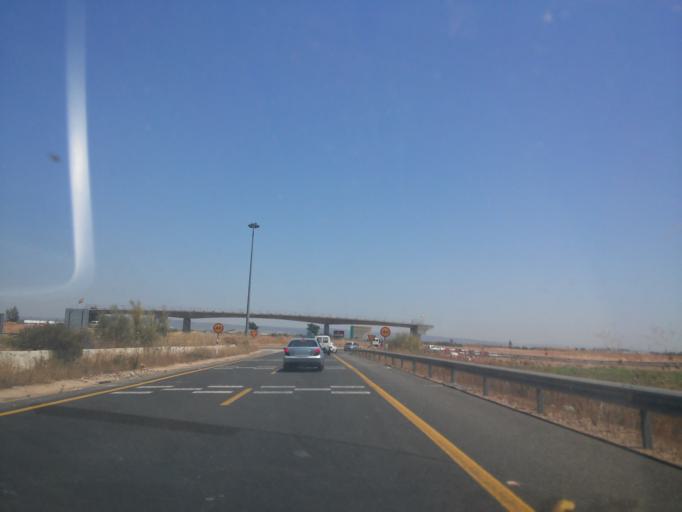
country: ES
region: Andalusia
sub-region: Provincia de Sevilla
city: La Rinconada
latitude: 37.4659
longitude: -5.9676
